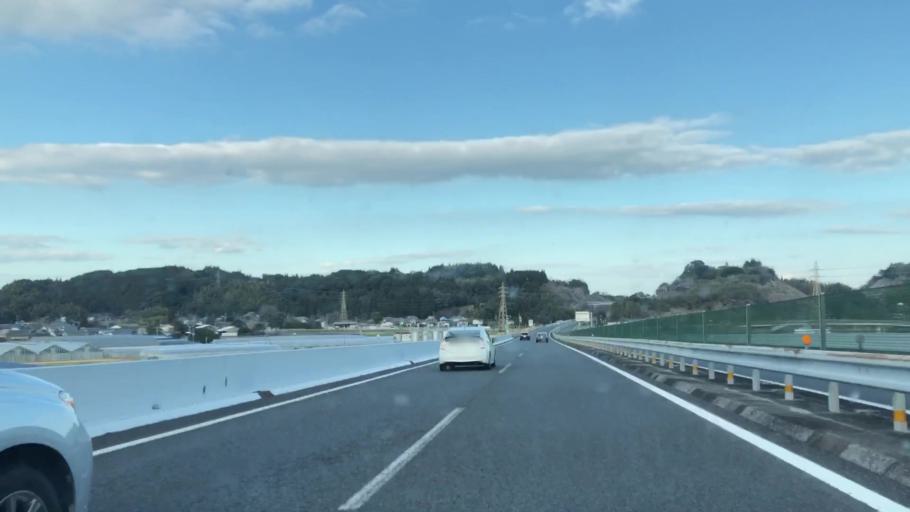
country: JP
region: Miyazaki
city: Miyazaki-shi
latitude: 31.8591
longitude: 131.3777
